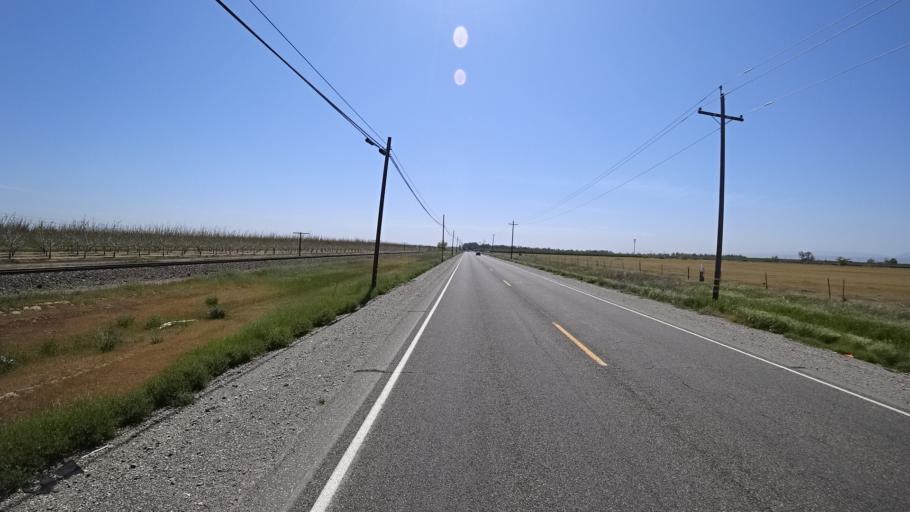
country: US
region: California
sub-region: Glenn County
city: Willows
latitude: 39.6092
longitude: -122.1940
